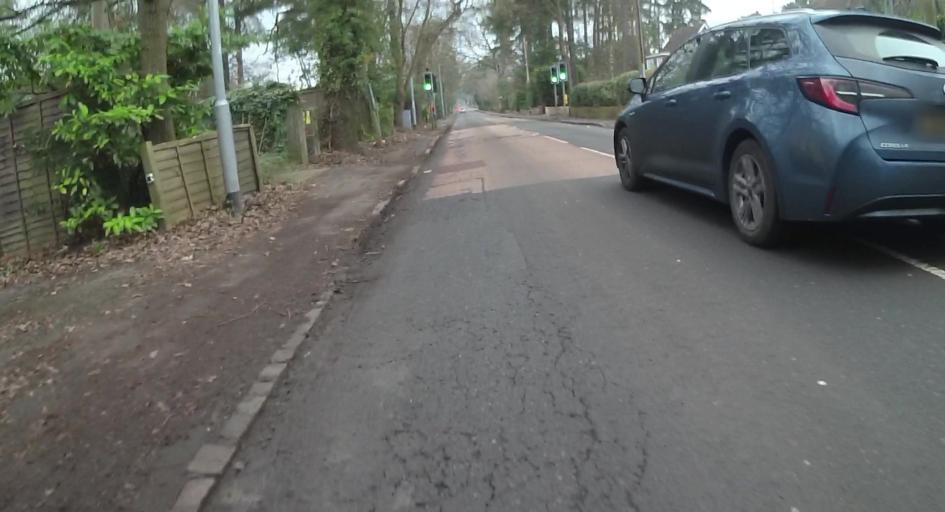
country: GB
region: England
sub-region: Wokingham
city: Finchampstead
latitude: 51.3801
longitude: -0.8545
